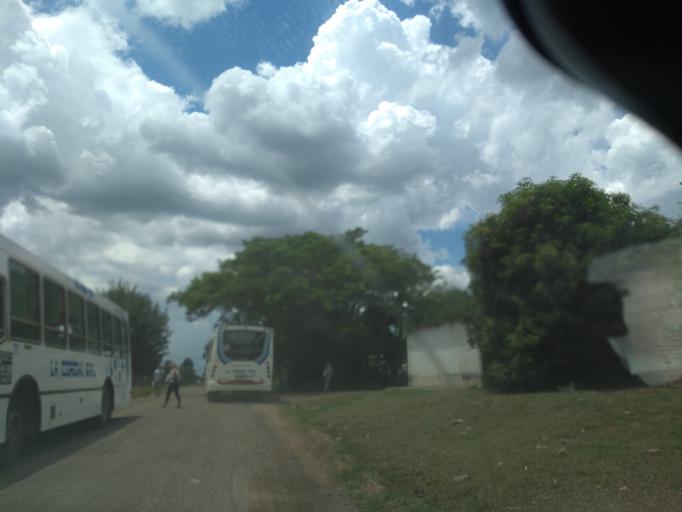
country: AR
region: Chaco
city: Fontana
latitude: -27.4071
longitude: -59.0464
